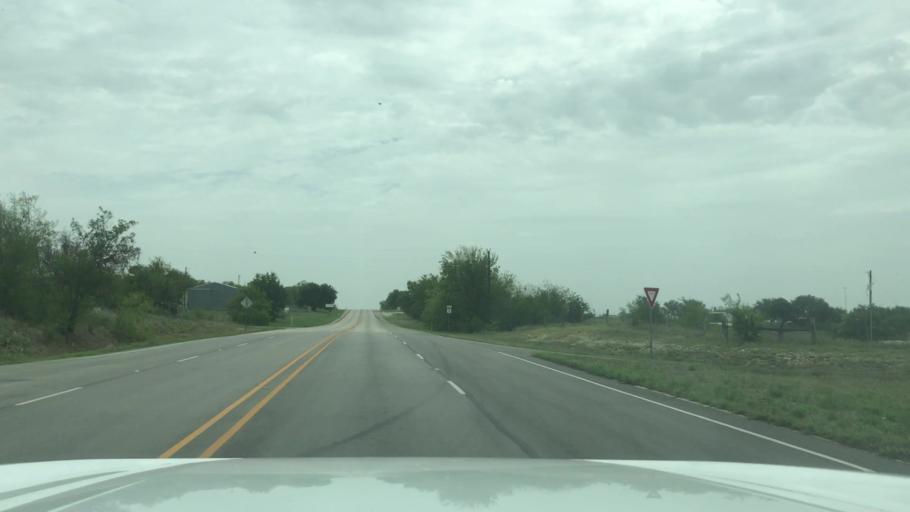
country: US
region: Texas
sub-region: Erath County
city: Dublin
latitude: 32.0589
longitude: -98.2064
